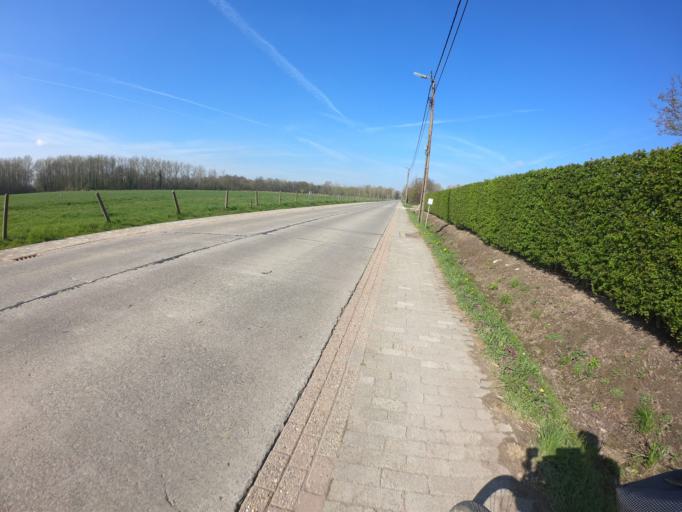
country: BE
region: Flanders
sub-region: Provincie Vlaams-Brabant
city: Geetbets
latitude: 50.8980
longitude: 5.1414
